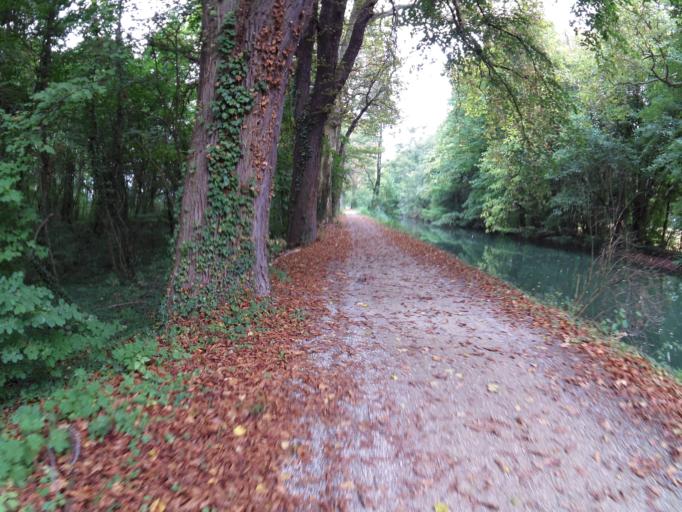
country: FR
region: Alsace
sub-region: Departement du Bas-Rhin
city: Marckolsheim
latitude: 48.1423
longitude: 7.5342
